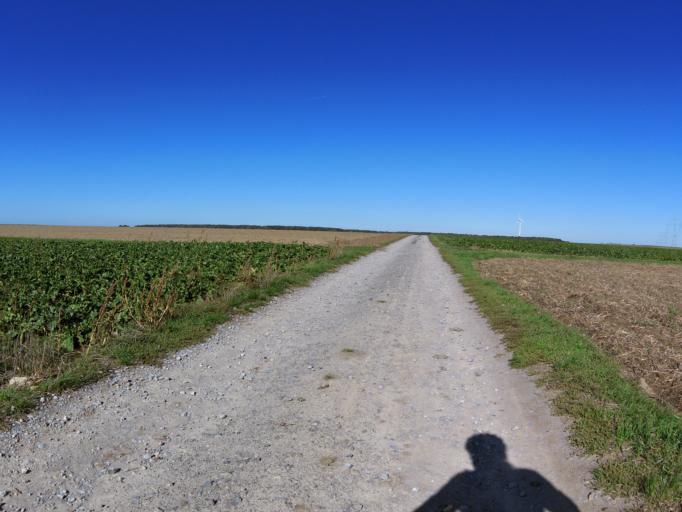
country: DE
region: Bavaria
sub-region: Regierungsbezirk Unterfranken
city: Theilheim
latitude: 49.7298
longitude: 10.0471
